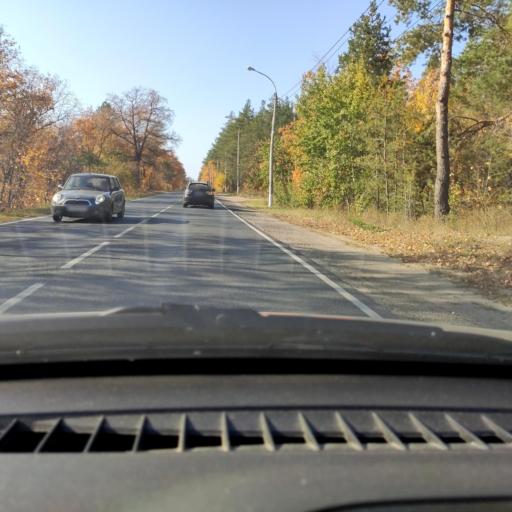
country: RU
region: Samara
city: Tol'yatti
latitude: 53.4734
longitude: 49.3996
